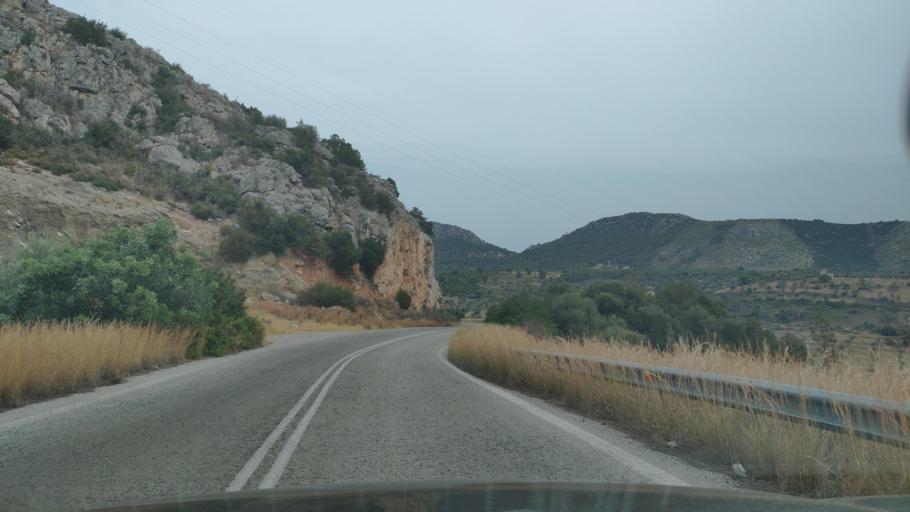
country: GR
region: Peloponnese
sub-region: Nomos Argolidos
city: Didyma
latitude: 37.4375
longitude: 23.1853
